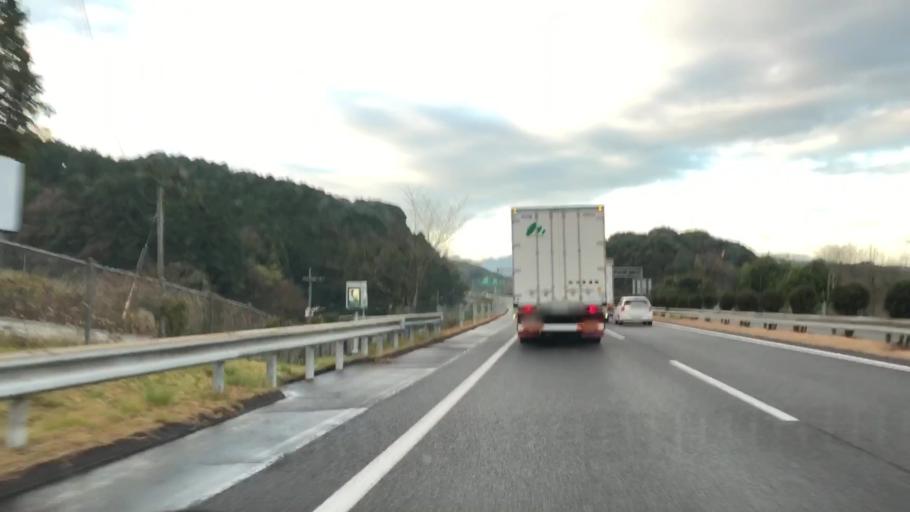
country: JP
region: Saga Prefecture
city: Takeocho-takeo
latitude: 33.1562
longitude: 130.0051
